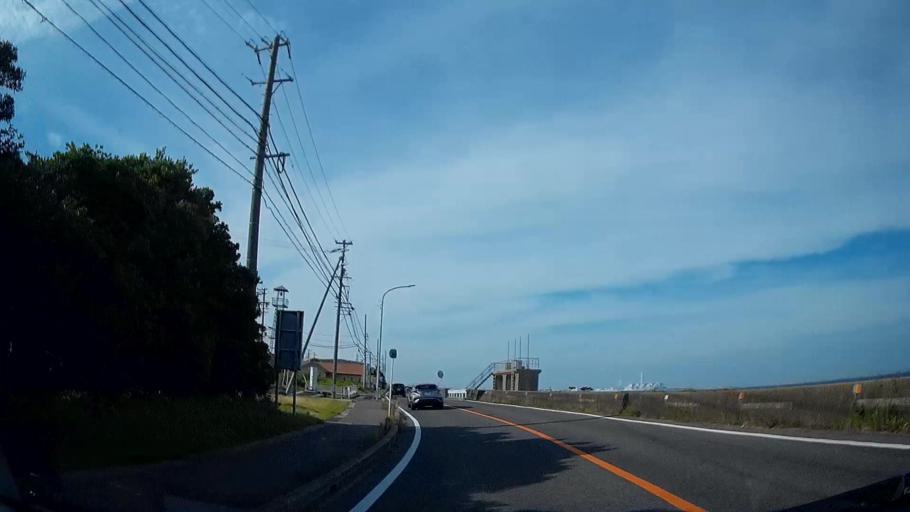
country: JP
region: Aichi
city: Taketoyo
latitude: 34.7930
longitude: 136.9205
